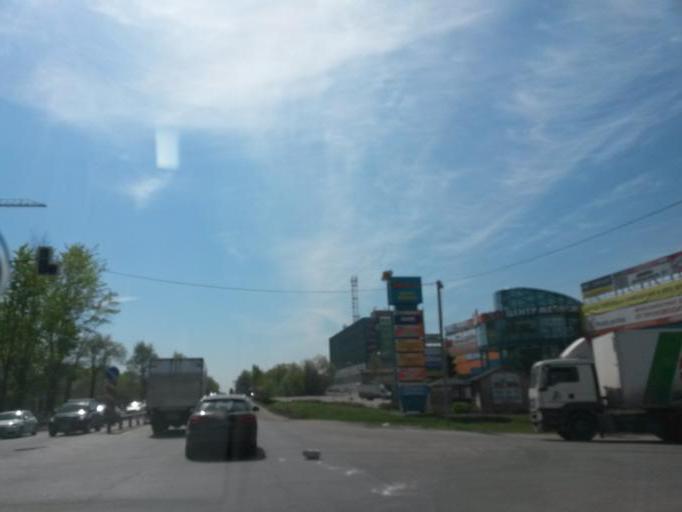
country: RU
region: Moskovskaya
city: Shcherbinka
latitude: 55.4827
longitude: 37.5658
